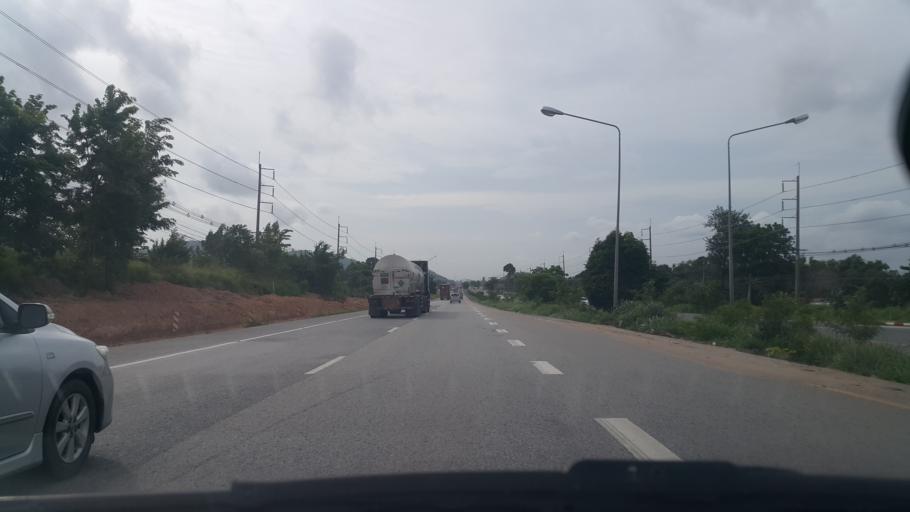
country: TH
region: Rayong
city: Nikhom Phattana
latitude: 12.7944
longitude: 101.1527
